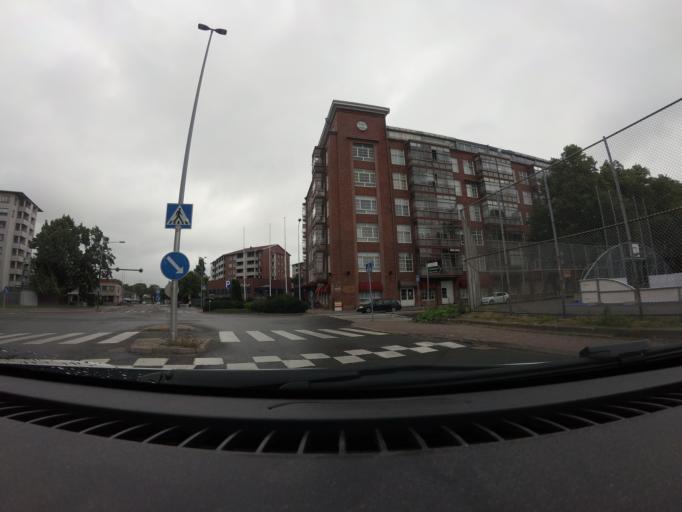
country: FI
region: Varsinais-Suomi
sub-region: Turku
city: Turku
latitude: 60.4575
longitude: 22.2724
